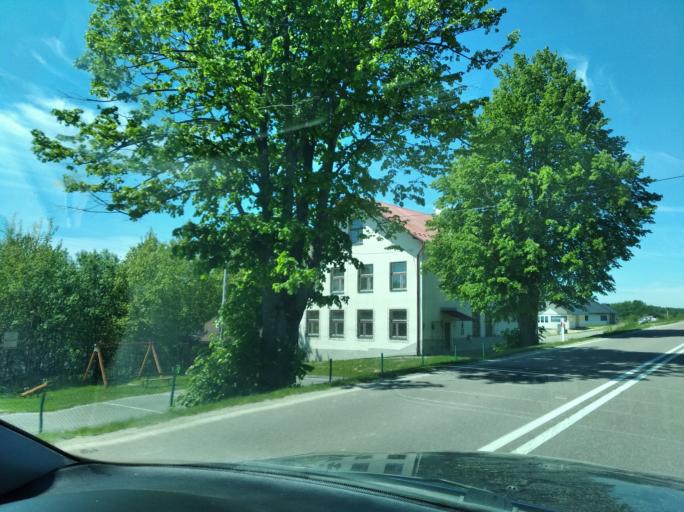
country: PL
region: Subcarpathian Voivodeship
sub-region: Powiat strzyzowski
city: Gwoznica Gorna
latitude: 49.8150
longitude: 21.9935
